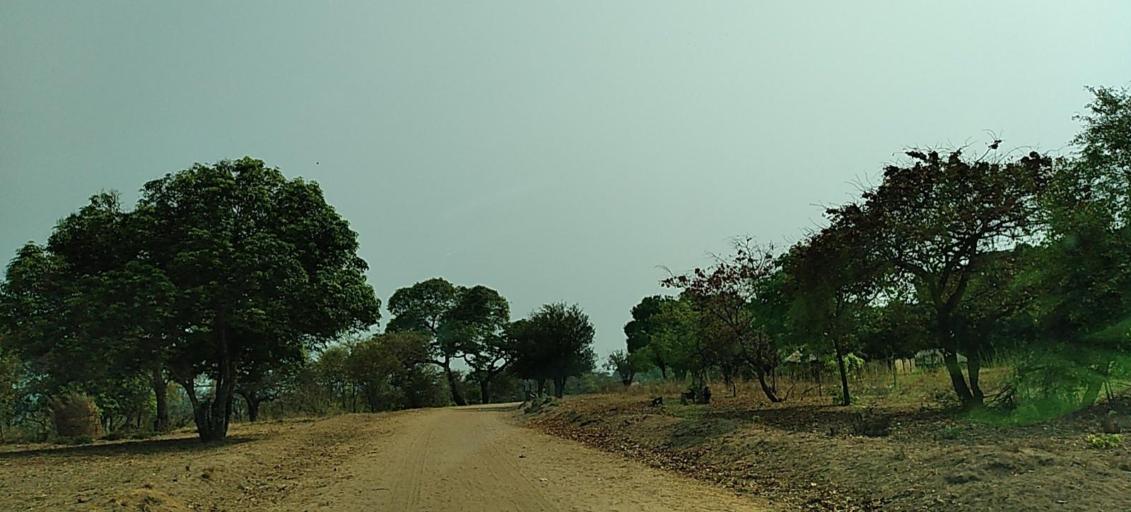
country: ZM
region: North-Western
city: Zambezi
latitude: -13.1803
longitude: 23.4007
